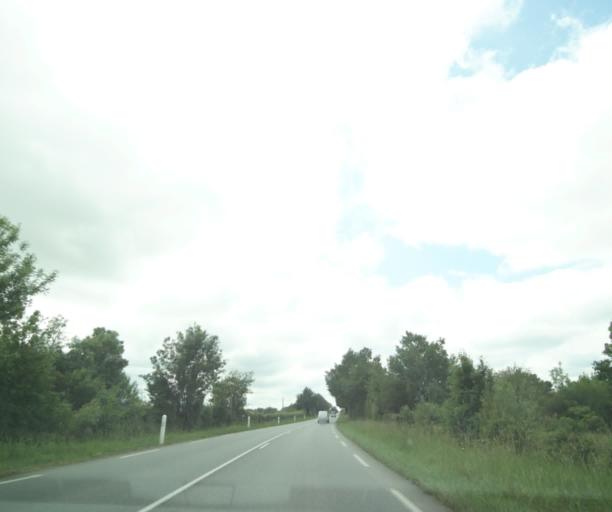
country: FR
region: Poitou-Charentes
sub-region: Departement des Deux-Sevres
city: Viennay
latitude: 46.7037
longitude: -0.2390
